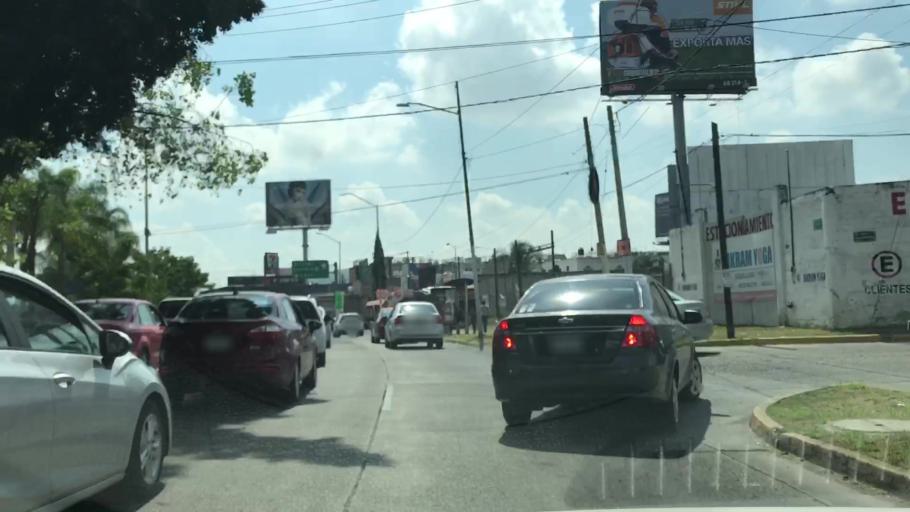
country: MX
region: Jalisco
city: Guadalajara
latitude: 20.6393
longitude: -103.4197
